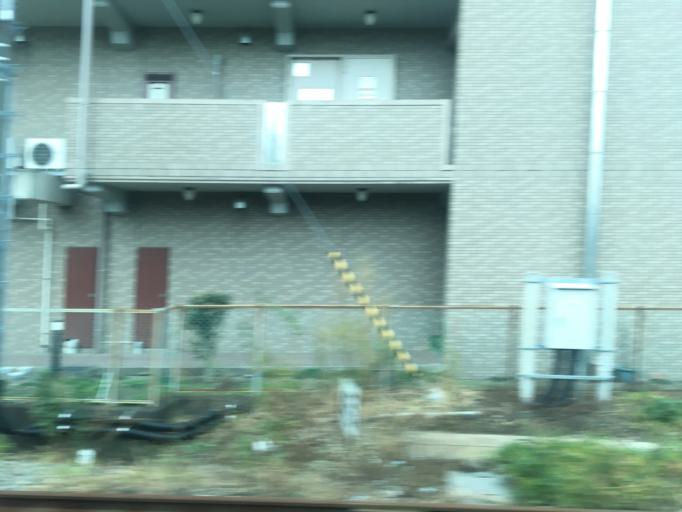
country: JP
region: Saitama
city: Okegawa
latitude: 36.0011
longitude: 139.5613
